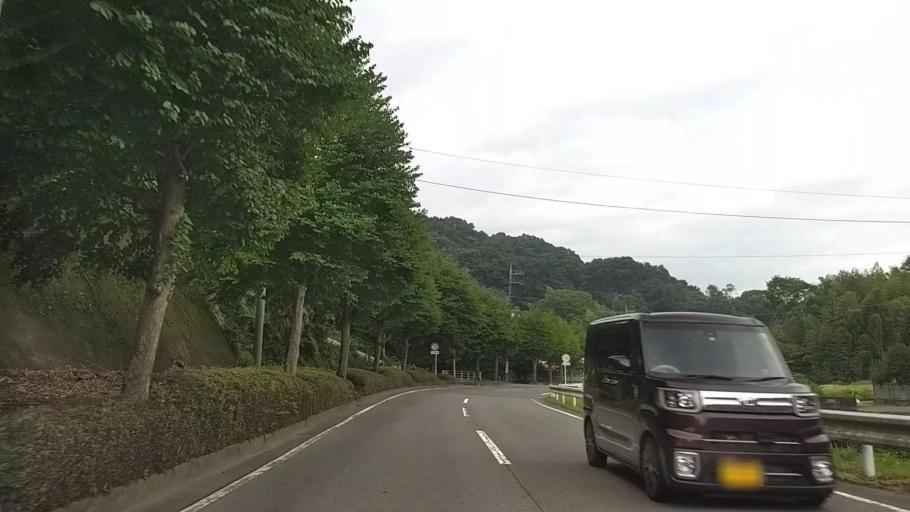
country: JP
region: Kanagawa
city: Hadano
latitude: 35.3352
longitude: 139.1991
